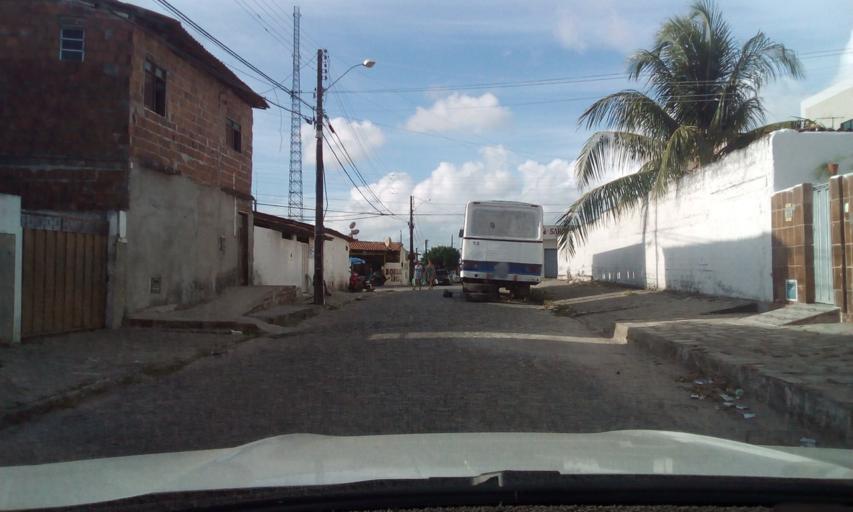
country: BR
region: Paraiba
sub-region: Joao Pessoa
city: Joao Pessoa
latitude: -7.1087
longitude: -34.8581
